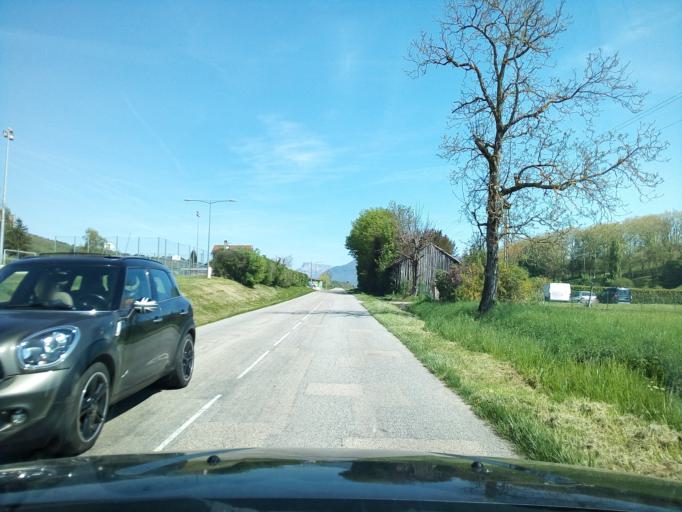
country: FR
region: Rhone-Alpes
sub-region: Departement de l'Isere
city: Barraux
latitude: 45.4322
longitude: 5.9818
